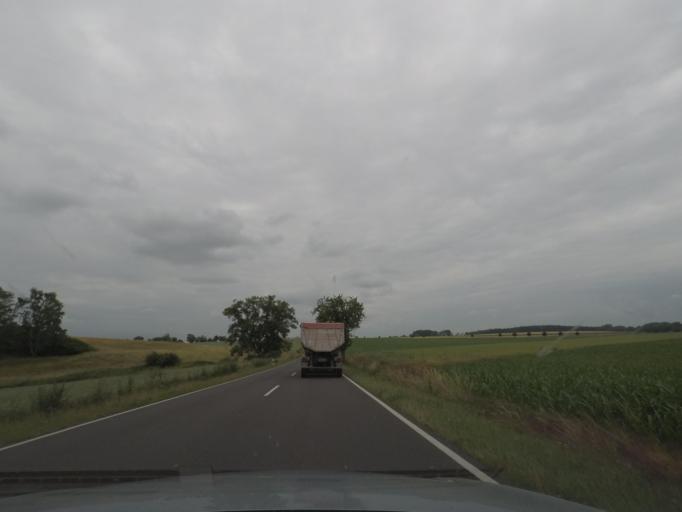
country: DE
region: Saxony-Anhalt
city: Suplingen
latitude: 52.2255
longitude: 11.3091
